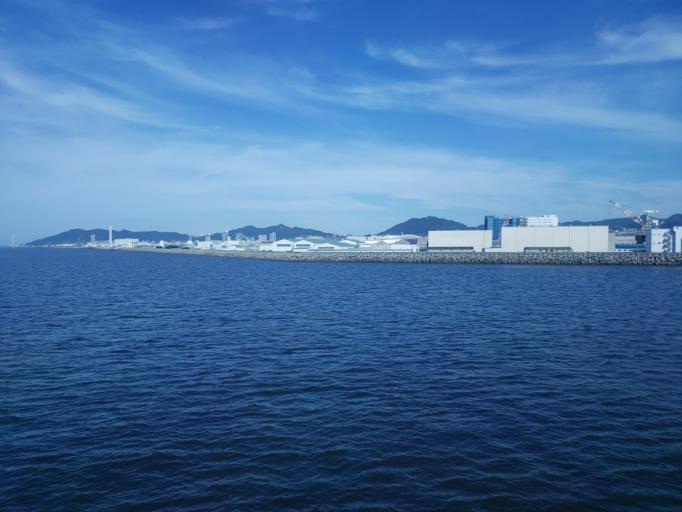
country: JP
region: Hyogo
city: Kobe
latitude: 34.6484
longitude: 135.1880
